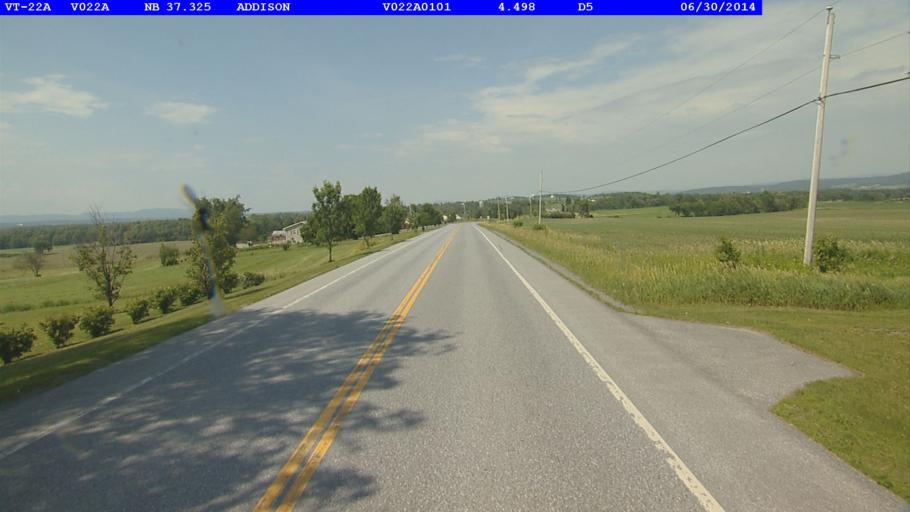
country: US
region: Vermont
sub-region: Addison County
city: Vergennes
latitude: 44.0942
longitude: -73.3009
